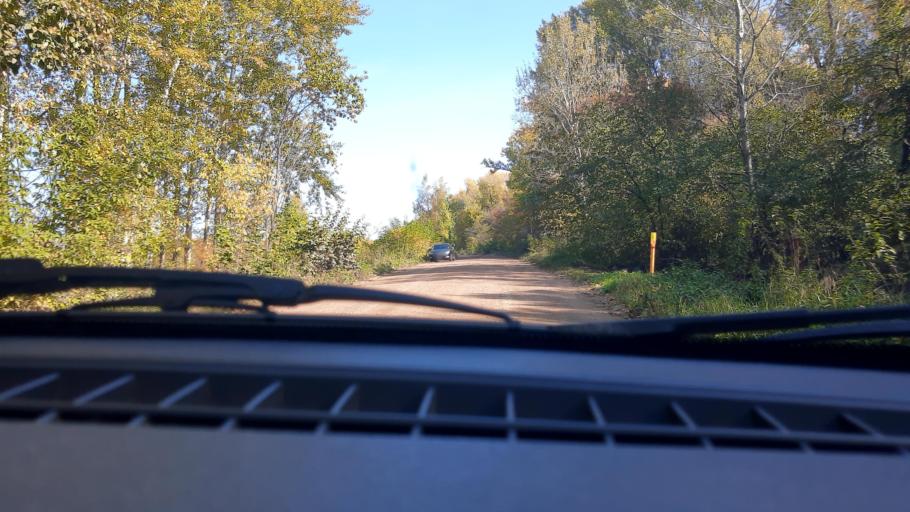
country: RU
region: Bashkortostan
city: Mikhaylovka
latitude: 54.7401
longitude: 55.8508
